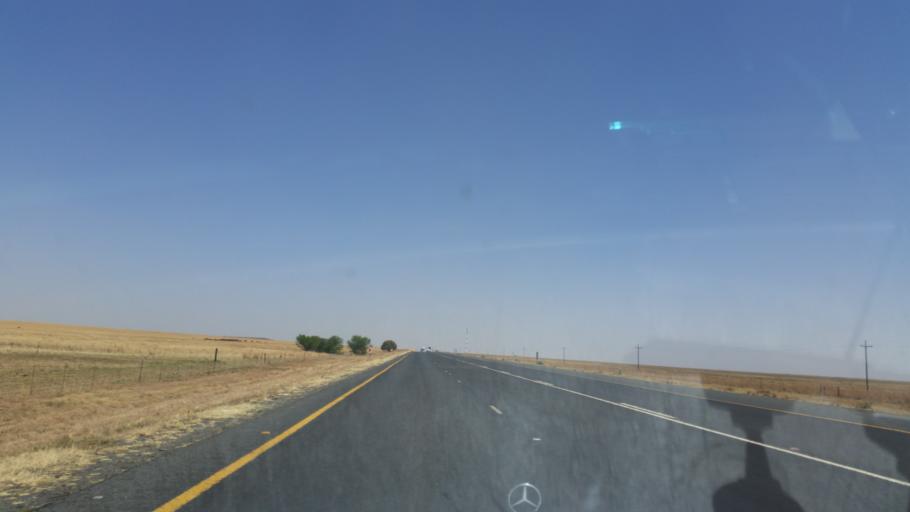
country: ZA
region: Orange Free State
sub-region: Lejweleputswa District Municipality
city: Brandfort
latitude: -28.8045
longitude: 26.6830
